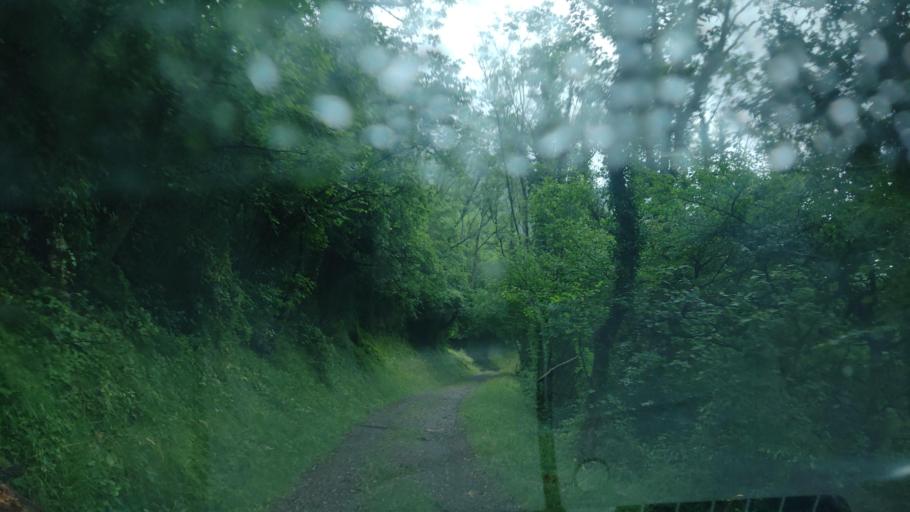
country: FR
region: Rhone-Alpes
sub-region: Departement de la Savoie
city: Coise-Saint-Jean-Pied-Gauthier
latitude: 45.4977
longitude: 6.1423
